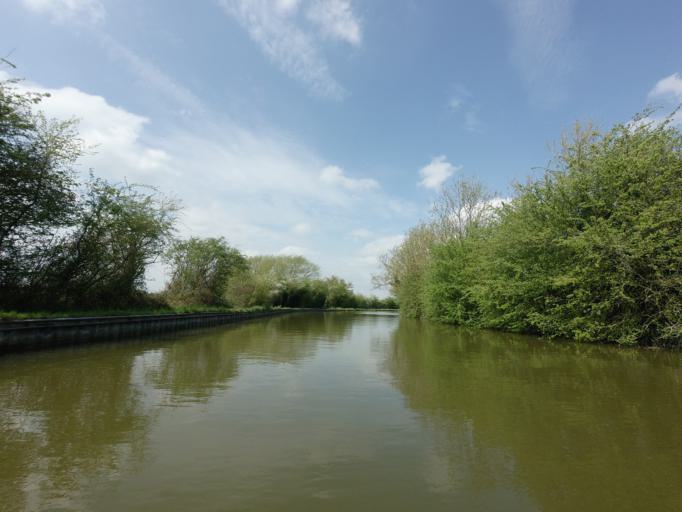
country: GB
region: England
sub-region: Buckinghamshire
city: Cheddington
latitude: 51.8803
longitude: -0.6593
